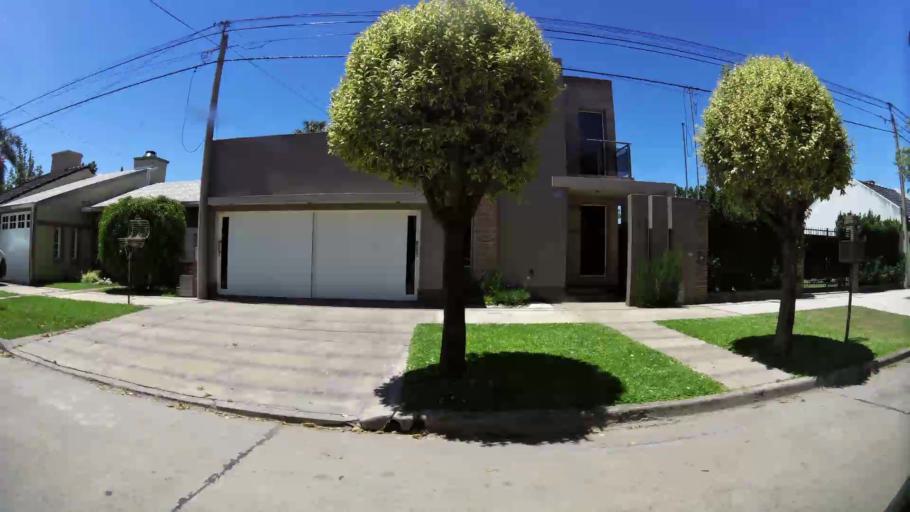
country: AR
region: Santa Fe
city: Rafaela
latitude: -31.2548
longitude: -61.4596
